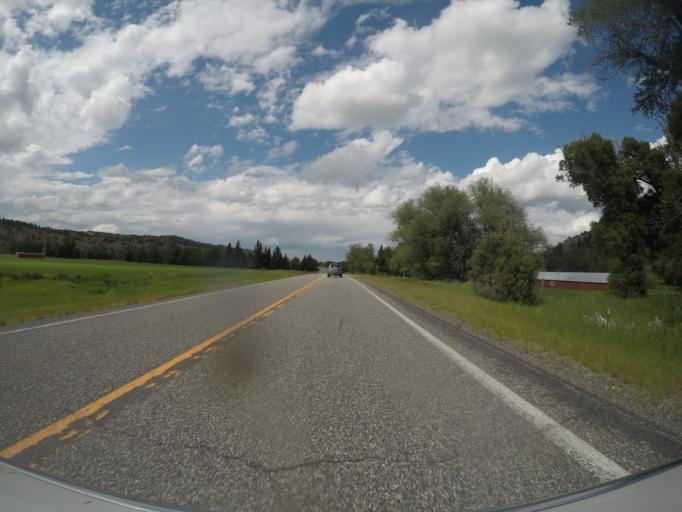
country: US
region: Montana
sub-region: Sweet Grass County
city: Big Timber
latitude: 45.7208
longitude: -109.9970
